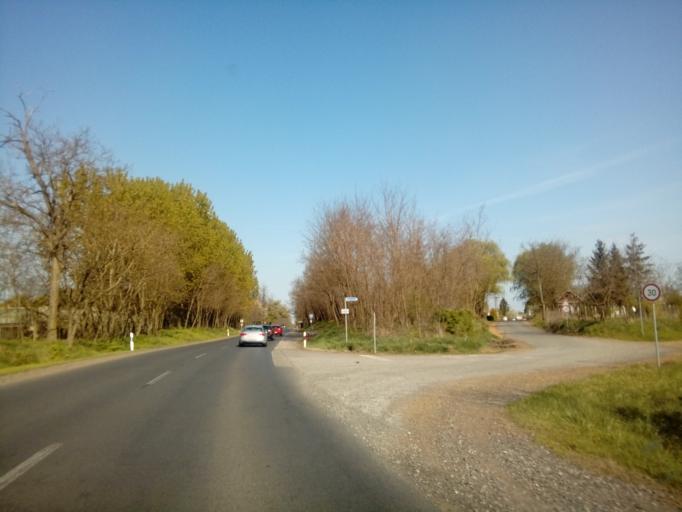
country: HU
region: Szabolcs-Szatmar-Bereg
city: Nagykallo
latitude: 47.8992
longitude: 21.7933
